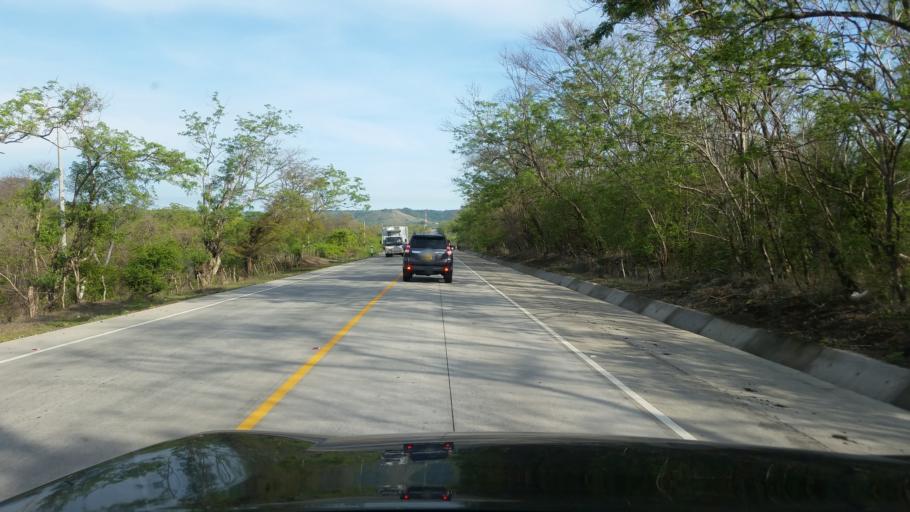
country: NI
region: Leon
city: Nagarote
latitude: 12.1213
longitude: -86.6275
